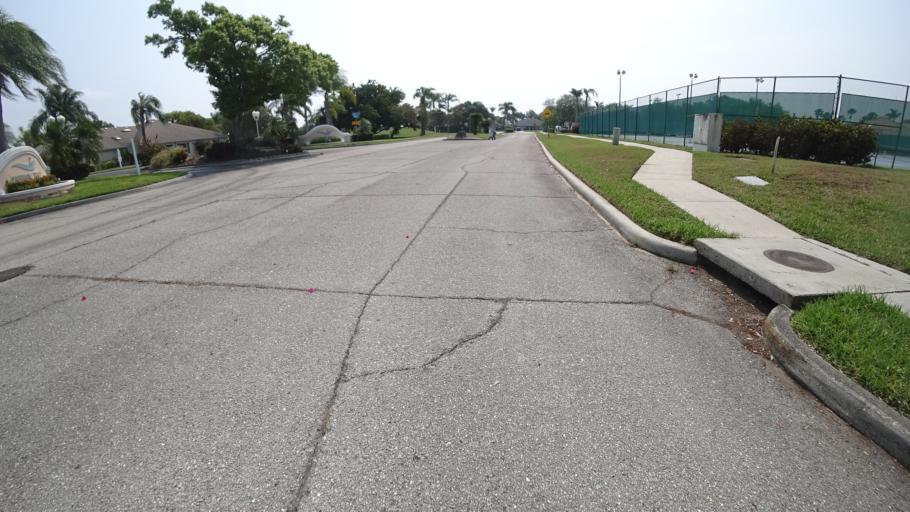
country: US
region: Florida
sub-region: Manatee County
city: Samoset
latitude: 27.4549
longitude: -82.5107
